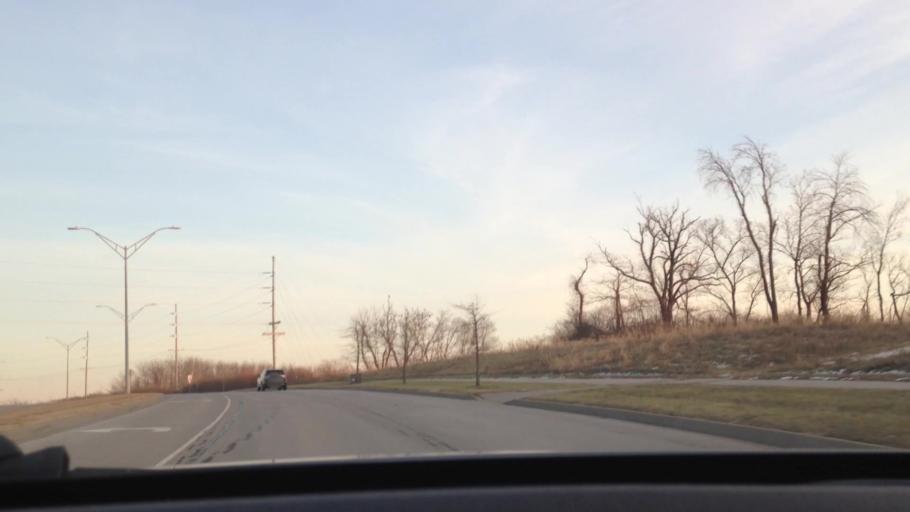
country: US
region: Missouri
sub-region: Clay County
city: Pleasant Valley
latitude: 39.2098
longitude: -94.4672
